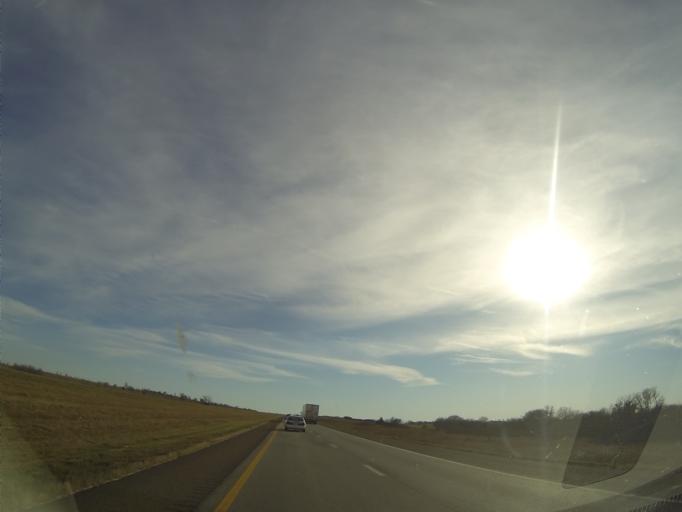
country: US
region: Kansas
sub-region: Ottawa County
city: Minneapolis
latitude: 38.9949
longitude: -97.6397
